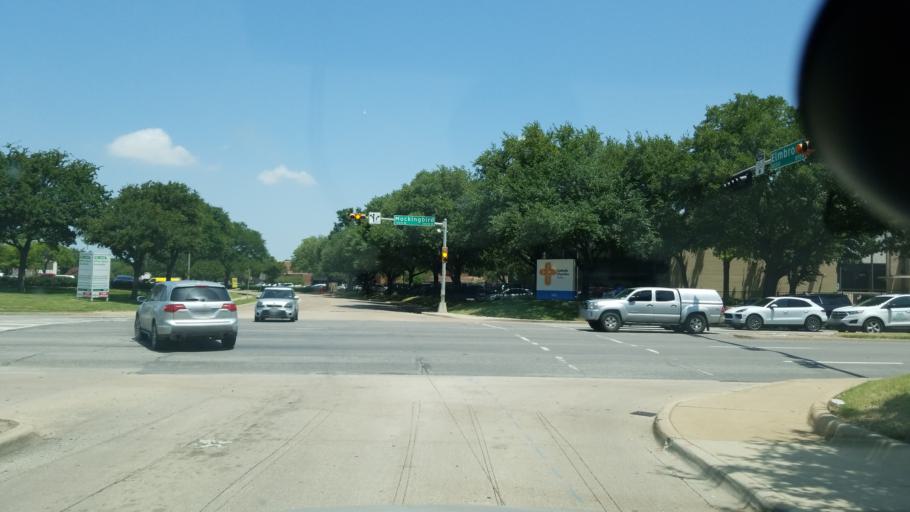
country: US
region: Texas
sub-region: Dallas County
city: Dallas
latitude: 32.8220
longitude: -96.8637
